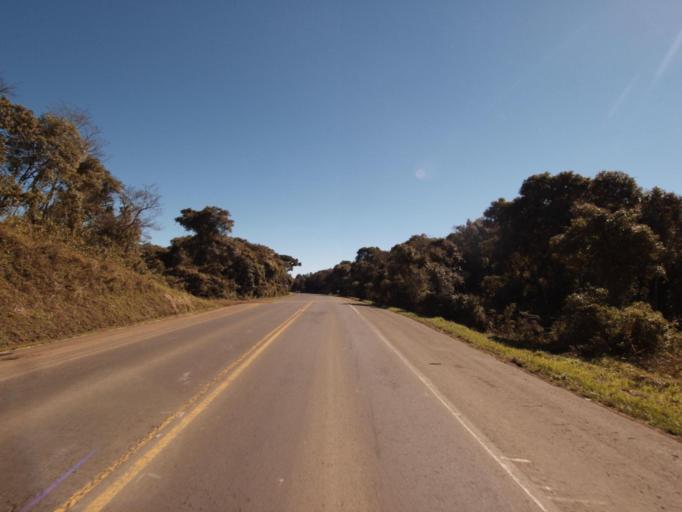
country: BR
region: Santa Catarina
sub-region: Joacaba
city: Joacaba
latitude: -27.1001
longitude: -51.6490
